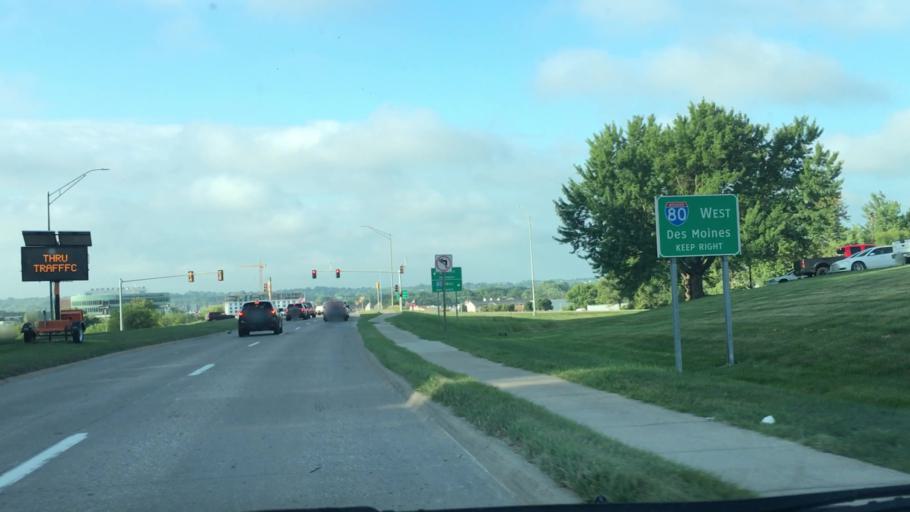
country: US
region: Iowa
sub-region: Johnson County
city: Coralville
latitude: 41.6879
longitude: -91.5643
